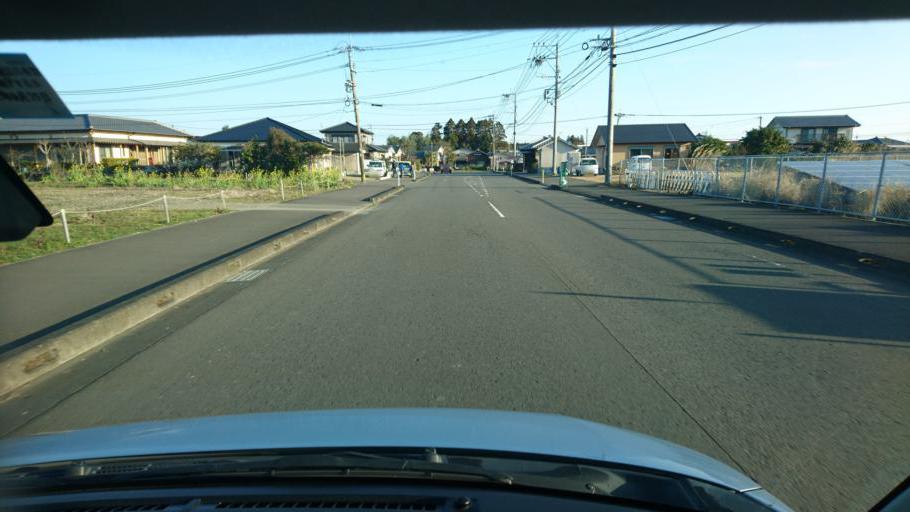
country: JP
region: Miyazaki
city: Miyazaki-shi
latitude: 31.8391
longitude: 131.4201
